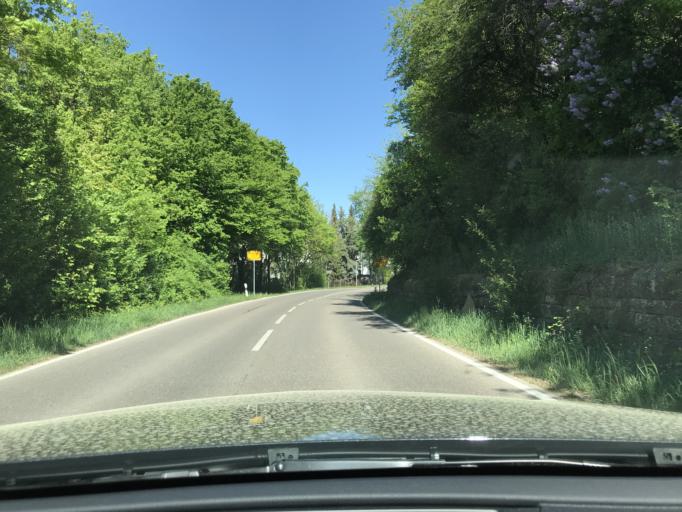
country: DE
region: Baden-Wuerttemberg
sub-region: Regierungsbezirk Stuttgart
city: Weinstadt-Endersbach
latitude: 48.8257
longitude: 9.3759
